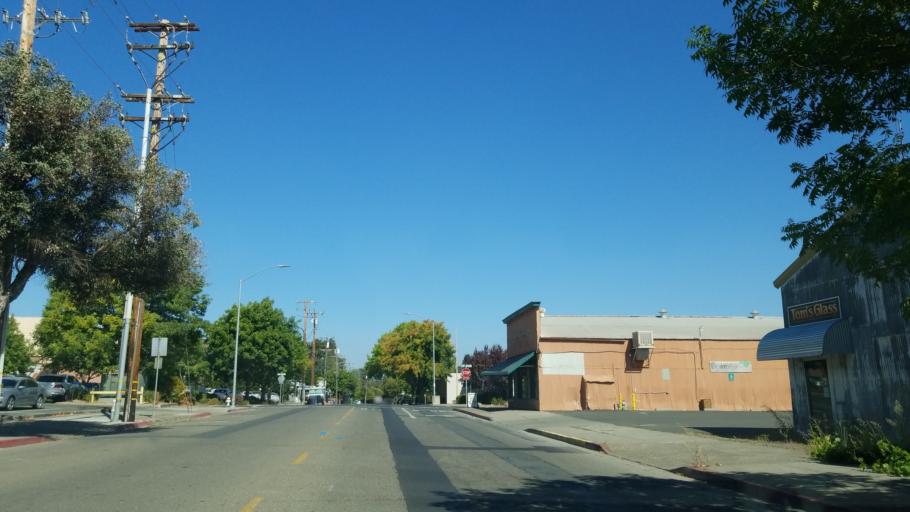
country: US
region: California
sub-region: Mendocino County
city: Ukiah
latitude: 39.1496
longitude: -123.2066
